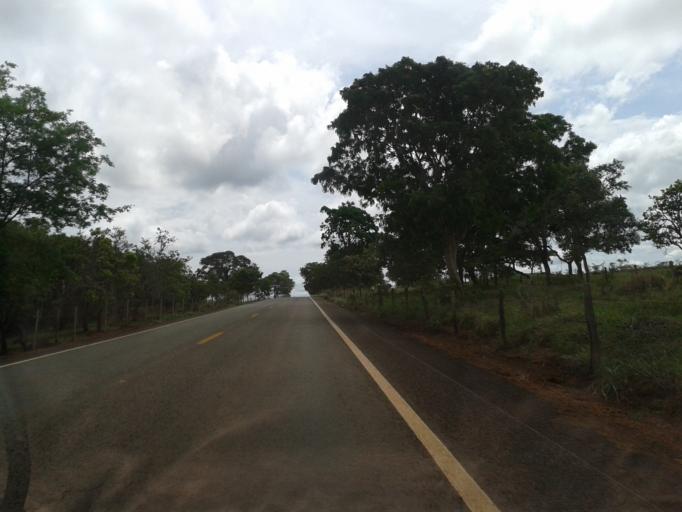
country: BR
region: Goias
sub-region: Buriti Alegre
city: Buriti Alegre
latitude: -18.1268
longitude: -49.1374
